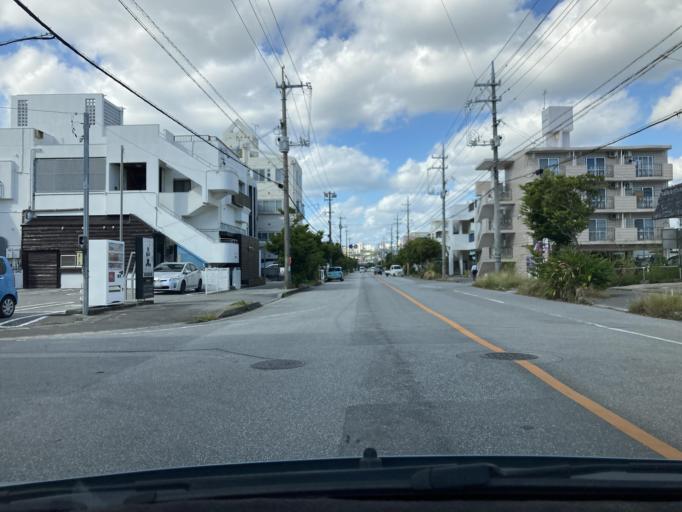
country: JP
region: Okinawa
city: Okinawa
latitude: 26.3202
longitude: 127.8352
